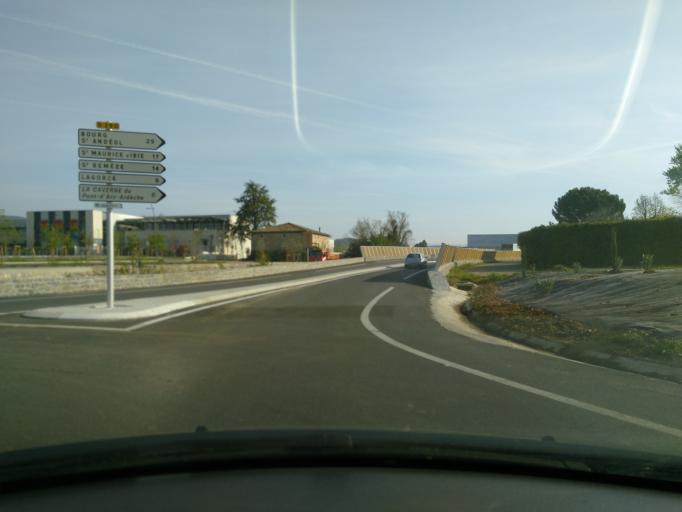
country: FR
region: Rhone-Alpes
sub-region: Departement de l'Ardeche
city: Ruoms
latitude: 44.4040
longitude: 4.3991
